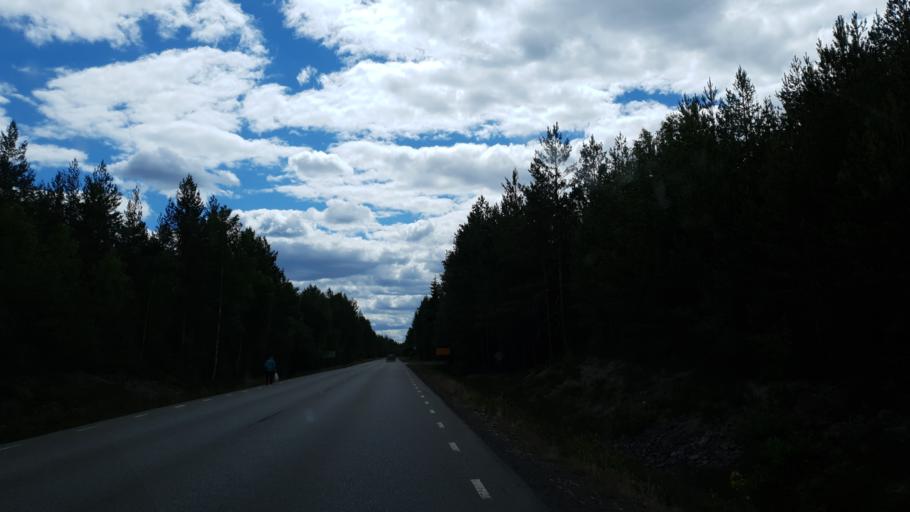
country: SE
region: Kronoberg
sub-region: Uppvidinge Kommun
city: Lenhovda
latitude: 56.9418
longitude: 15.5838
